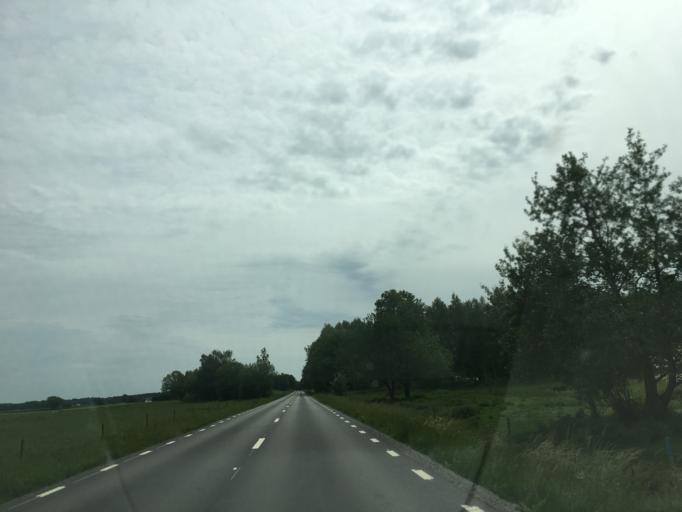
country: SE
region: Skane
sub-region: Sjobo Kommun
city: Blentarp
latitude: 55.5950
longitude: 13.5985
